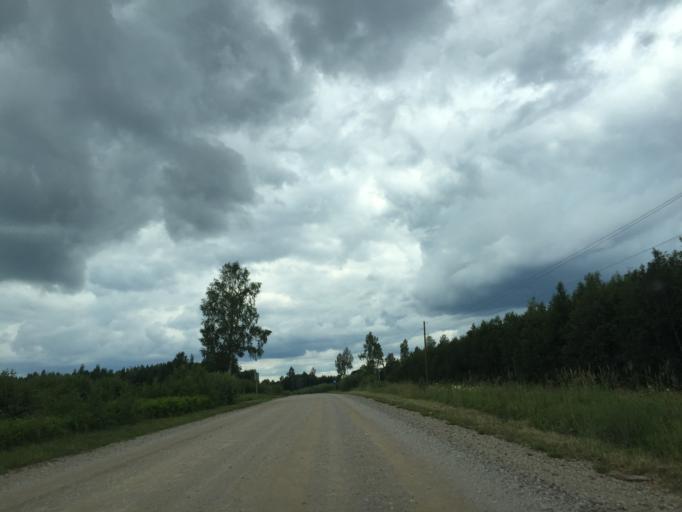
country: LV
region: Malpils
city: Malpils
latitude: 56.8754
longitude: 25.0013
